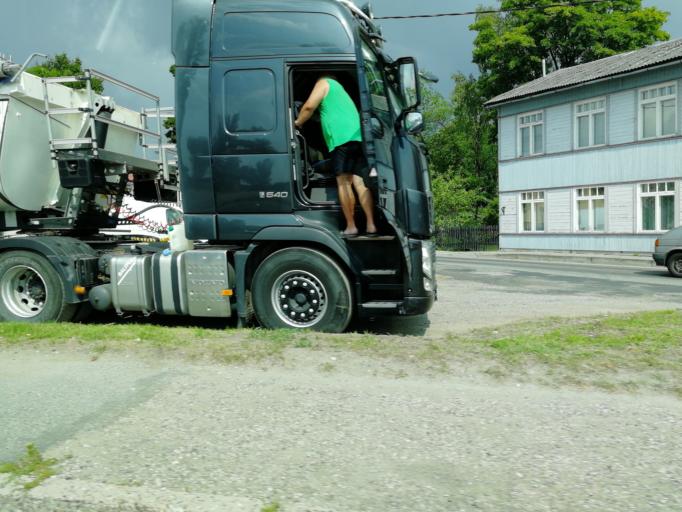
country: EE
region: Paernumaa
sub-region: Paernu linn
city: Parnu
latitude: 58.3917
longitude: 24.4998
